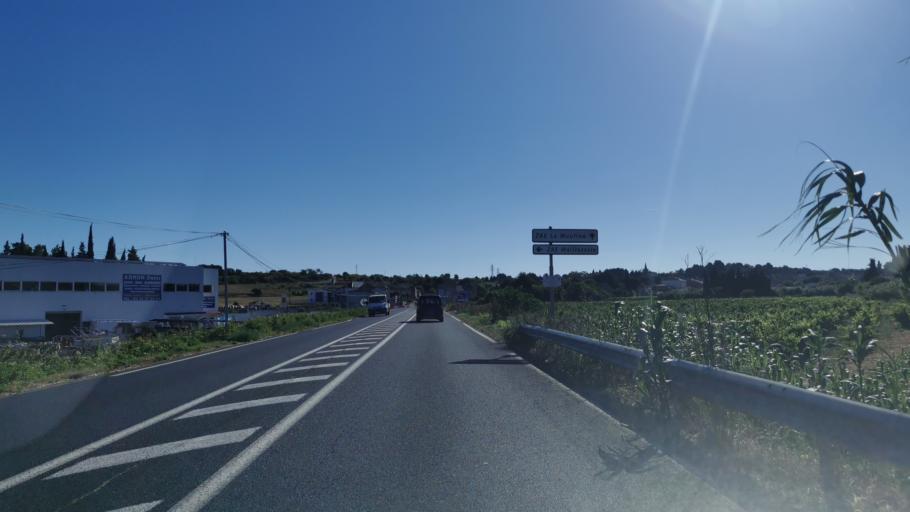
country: FR
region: Languedoc-Roussillon
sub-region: Departement de l'Herault
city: Nissan-lez-Enserune
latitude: 43.2900
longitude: 3.1165
